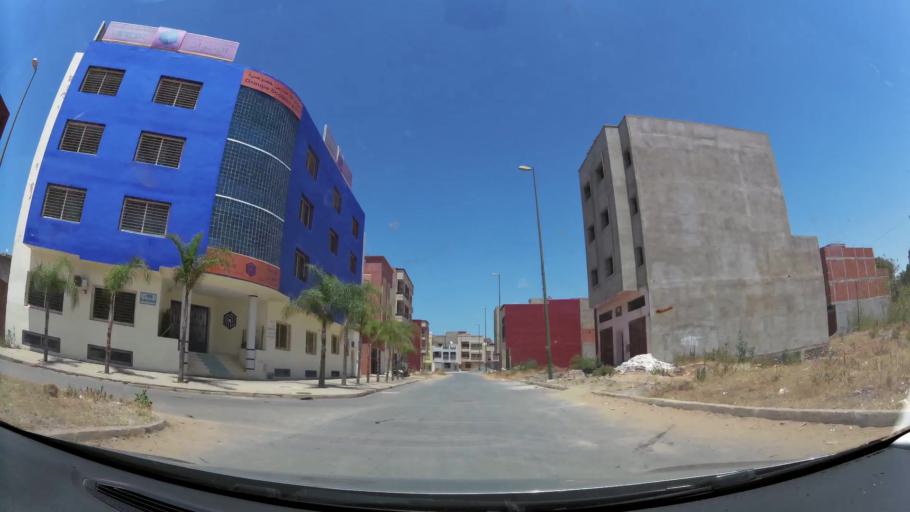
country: MA
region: Gharb-Chrarda-Beni Hssen
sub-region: Kenitra Province
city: Kenitra
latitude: 34.2325
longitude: -6.6056
